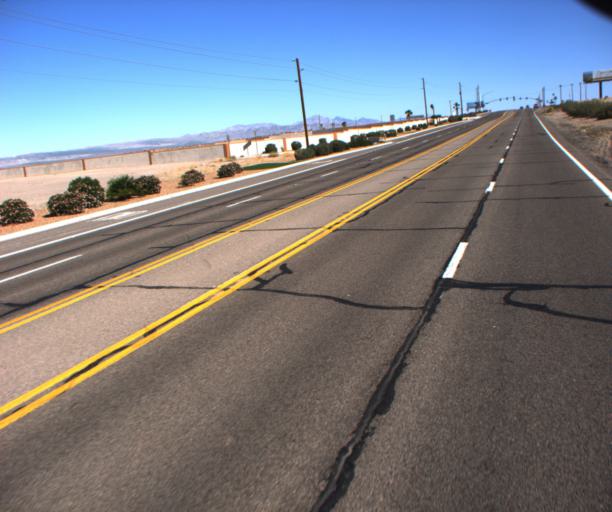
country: US
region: Arizona
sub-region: Mohave County
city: Mohave Valley
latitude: 34.9791
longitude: -114.5979
